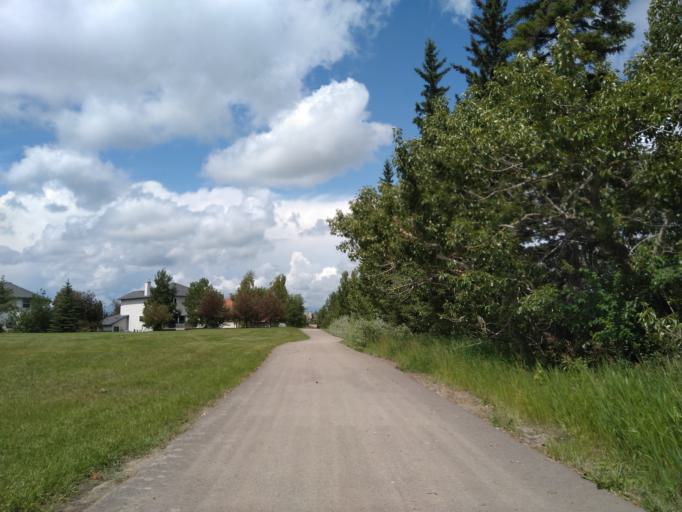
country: CA
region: Alberta
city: Cochrane
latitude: 51.1841
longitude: -114.4909
